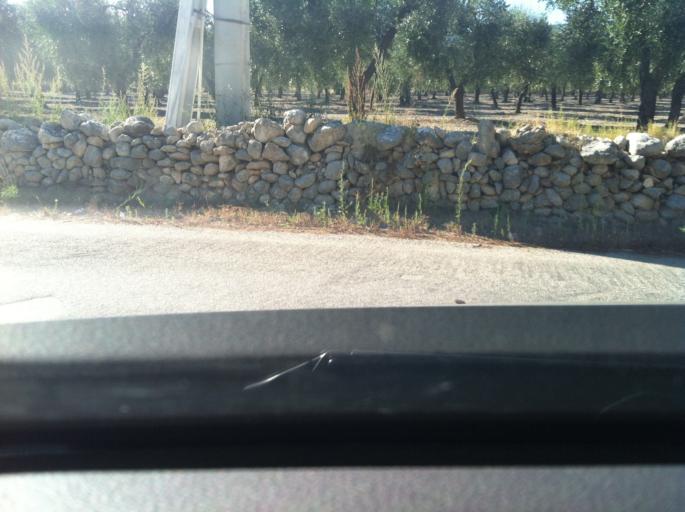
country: IT
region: Apulia
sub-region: Provincia di Foggia
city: Monte Sant'Angelo
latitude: 41.6588
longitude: 15.9755
